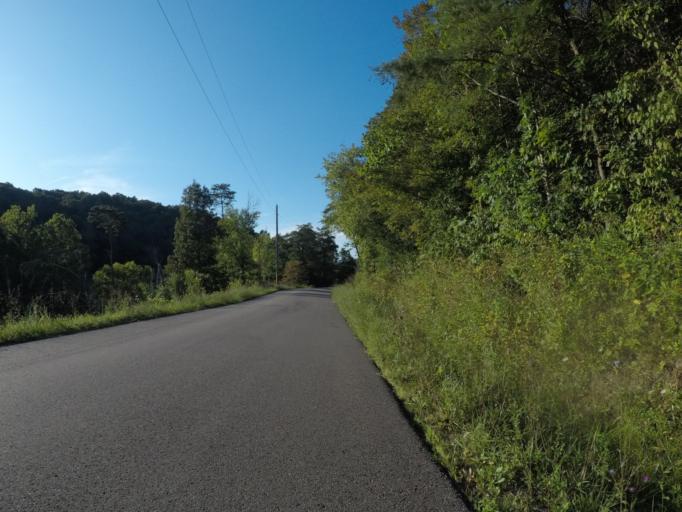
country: US
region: Ohio
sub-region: Lawrence County
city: Coal Grove
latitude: 38.5418
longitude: -82.5502
